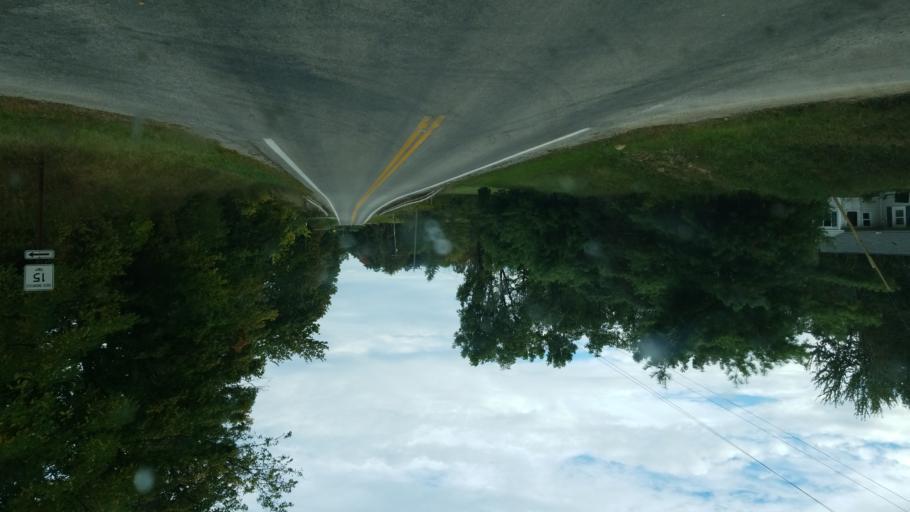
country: US
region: Ohio
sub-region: Knox County
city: Centerburg
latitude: 40.3622
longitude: -82.6900
